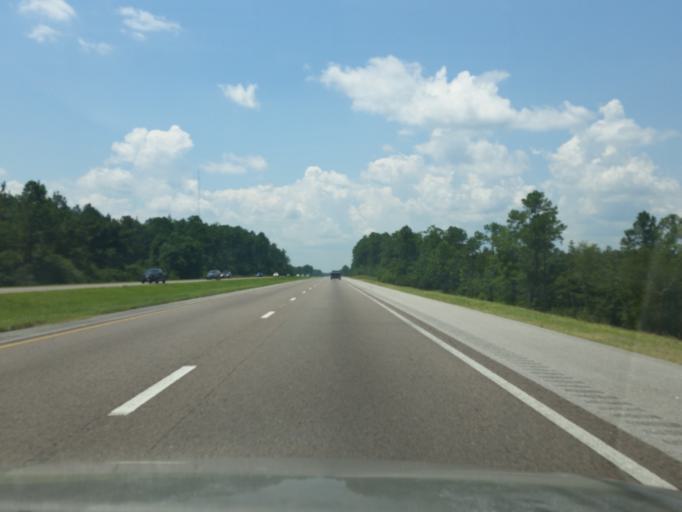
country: US
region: Alabama
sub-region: Baldwin County
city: Robertsdale
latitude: 30.5929
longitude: -87.5429
